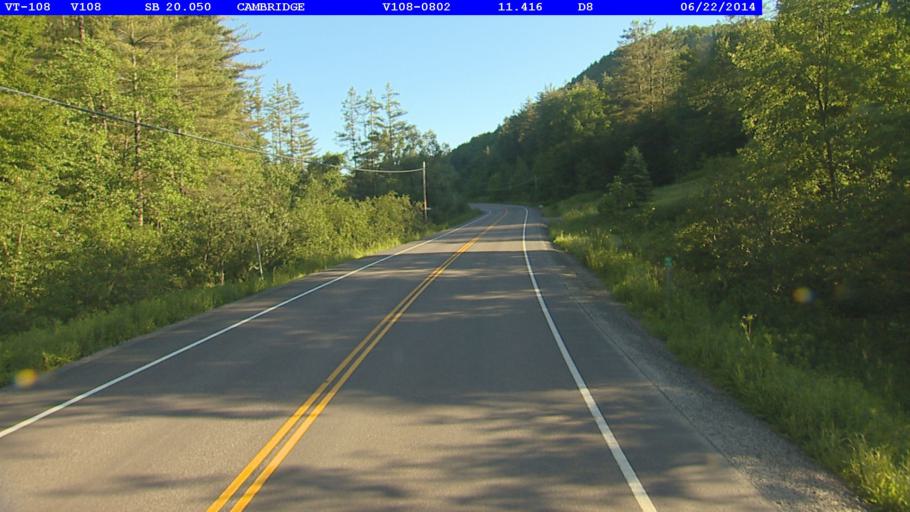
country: US
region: Vermont
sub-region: Lamoille County
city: Johnson
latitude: 44.6796
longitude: -72.8253
